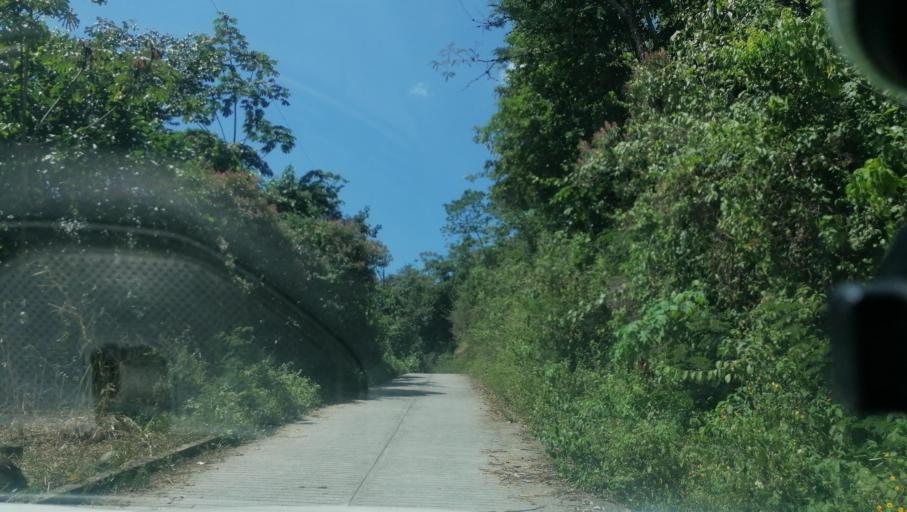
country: MX
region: Chiapas
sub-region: Union Juarez
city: Santo Domingo
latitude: 15.0658
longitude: -92.1392
